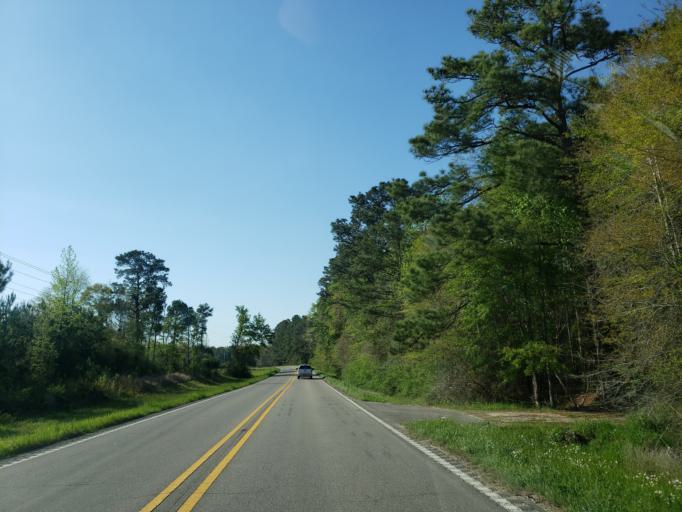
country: US
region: Mississippi
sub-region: Perry County
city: Richton
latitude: 31.4667
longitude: -88.9923
